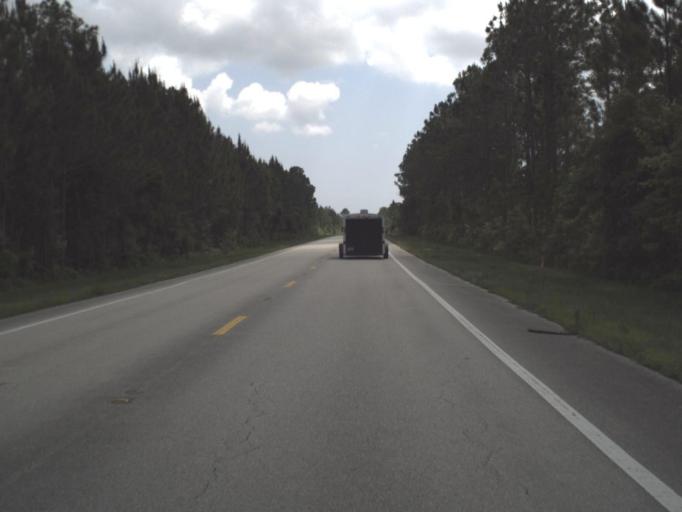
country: US
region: Florida
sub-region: Saint Johns County
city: Saint Augustine Shores
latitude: 29.7419
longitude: -81.3613
